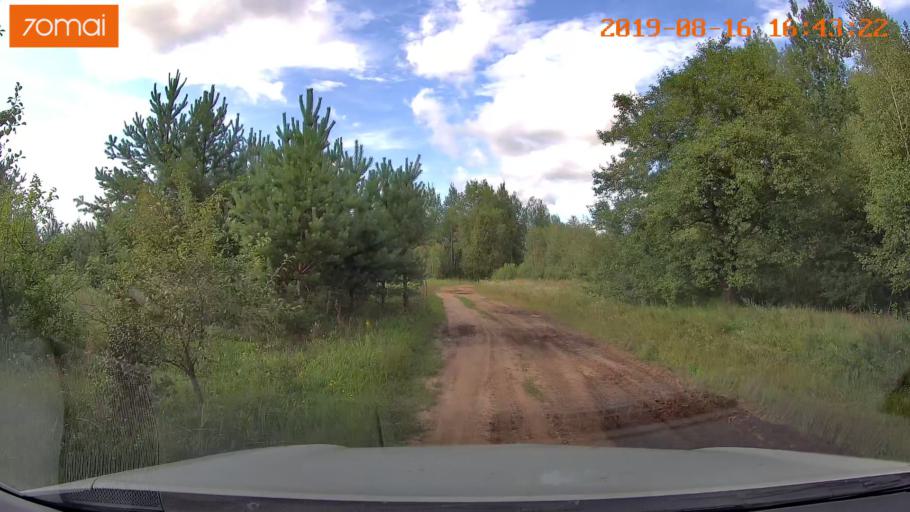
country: BY
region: Mogilev
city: Asipovichy
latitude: 53.2440
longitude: 28.7777
